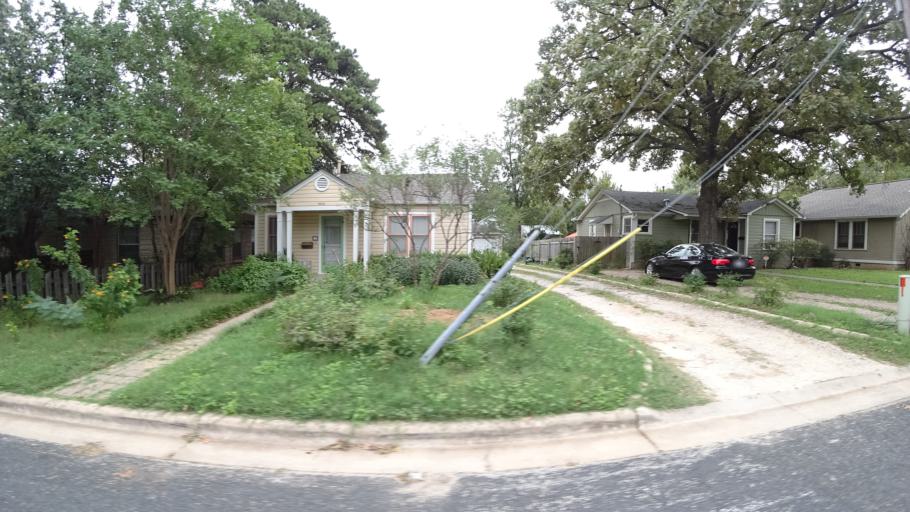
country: US
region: Texas
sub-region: Travis County
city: Austin
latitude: 30.2979
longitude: -97.7217
